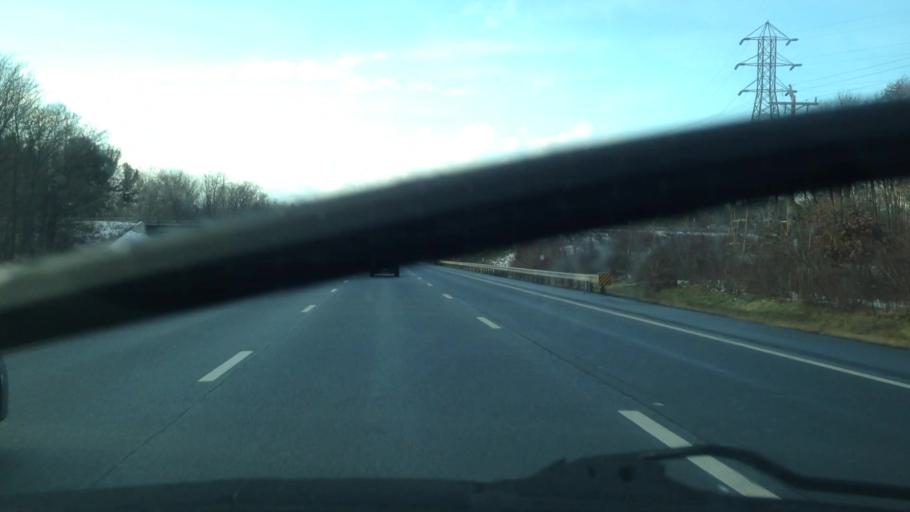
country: US
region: New York
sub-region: Schenectady County
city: Rotterdam
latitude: 42.7710
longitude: -73.9733
